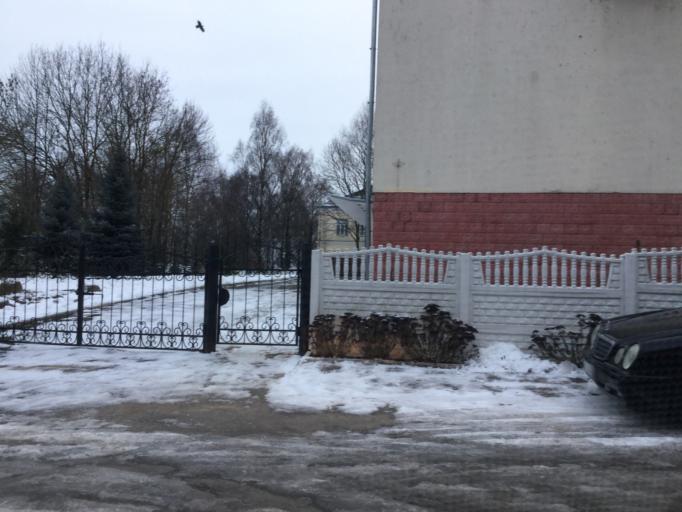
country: BY
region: Vitebsk
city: Vitebsk
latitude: 55.1968
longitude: 30.2173
